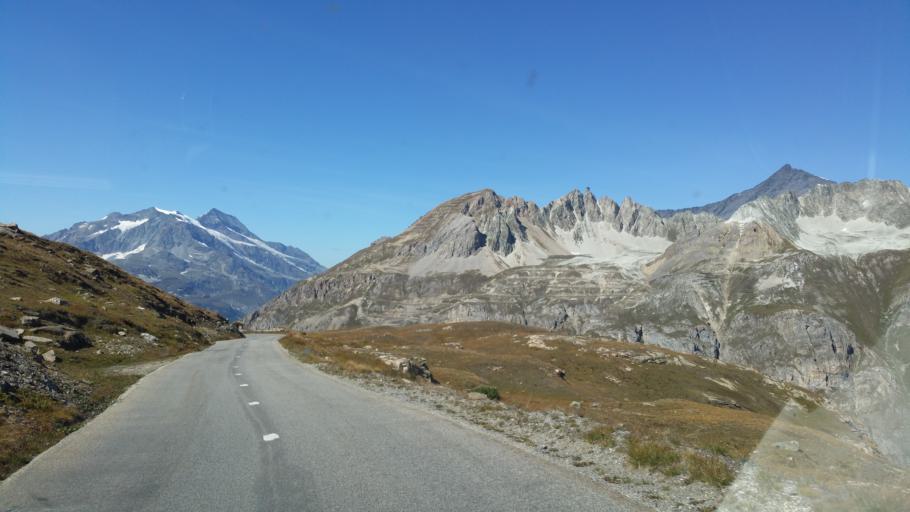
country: FR
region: Rhone-Alpes
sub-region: Departement de la Savoie
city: Val-d'Isere
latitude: 45.4363
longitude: 7.0137
